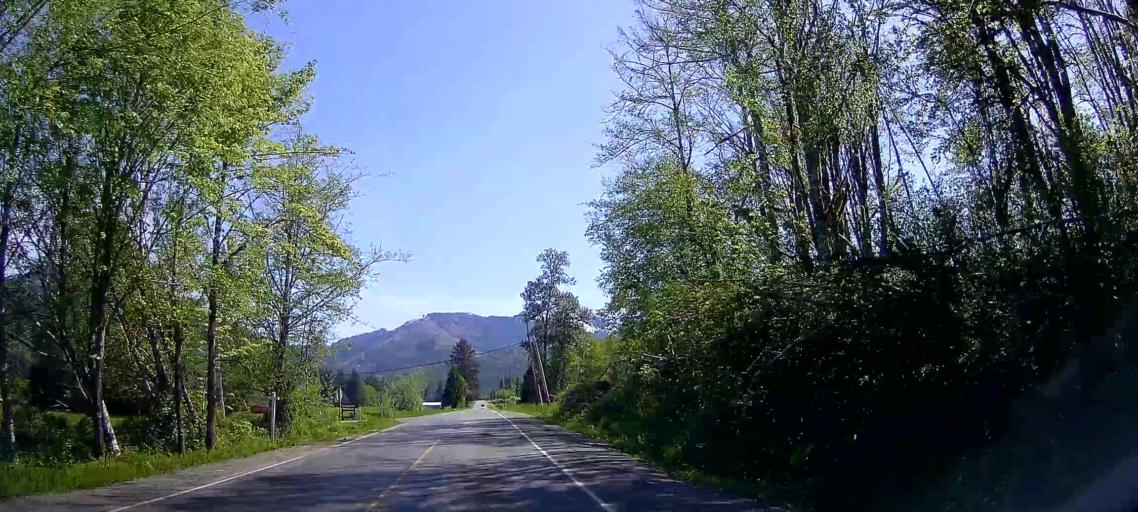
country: US
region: Washington
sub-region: Snohomish County
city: Darrington
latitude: 48.5186
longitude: -121.7400
